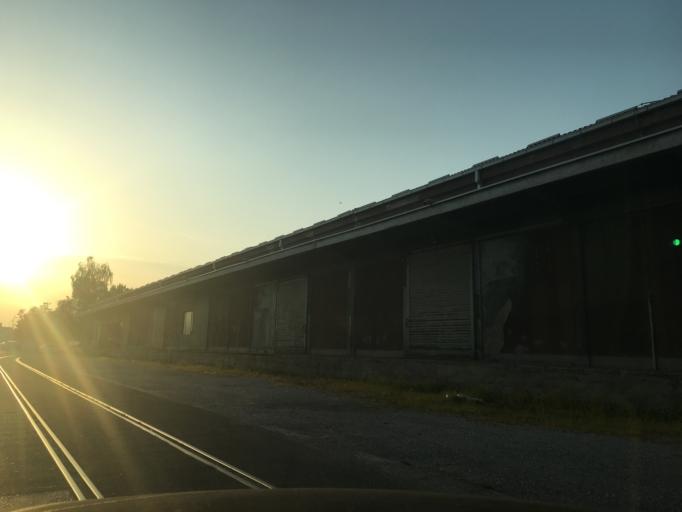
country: HR
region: Grad Zagreb
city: Novi Zagreb
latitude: 45.7805
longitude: 15.9682
